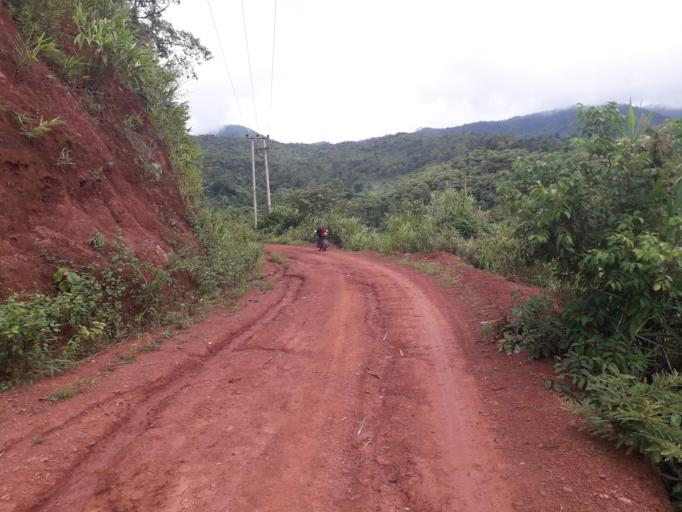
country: CN
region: Yunnan
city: Menglie
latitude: 22.2275
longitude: 101.6247
